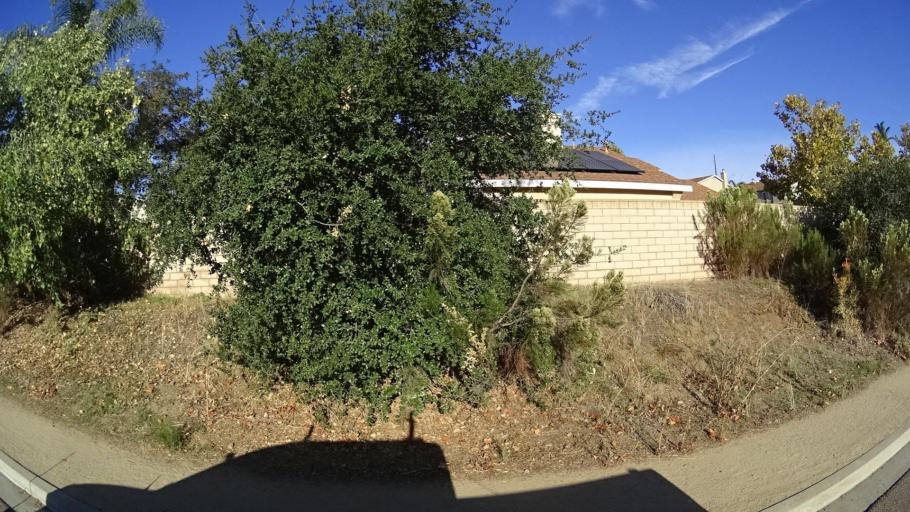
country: US
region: California
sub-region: San Diego County
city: Lakeside
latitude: 32.8488
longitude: -116.9048
